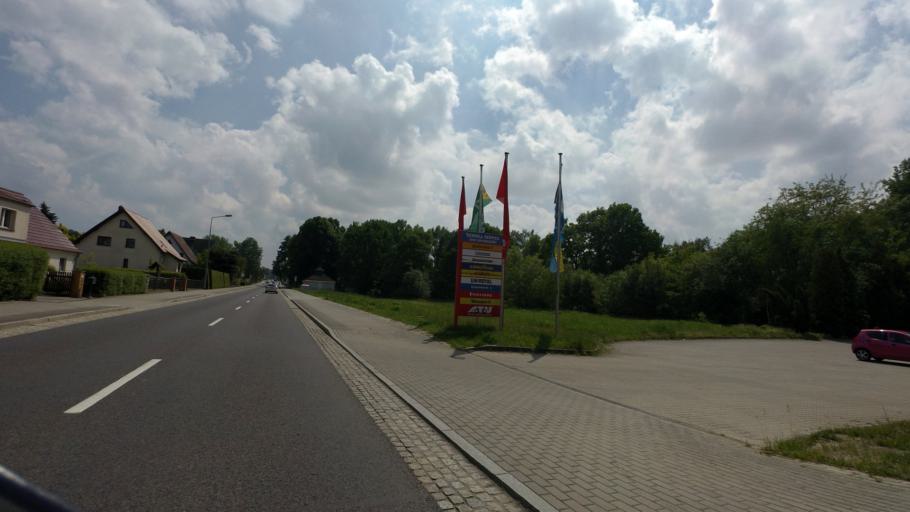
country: DE
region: Saxony
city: Weisswasser
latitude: 51.5151
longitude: 14.6102
